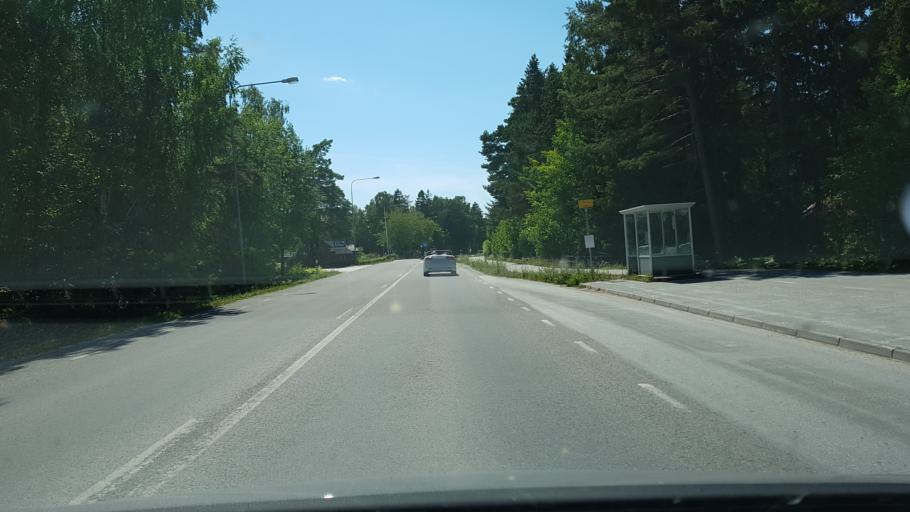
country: SE
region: Gotland
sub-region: Gotland
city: Klintehamn
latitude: 57.4894
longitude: 18.1422
